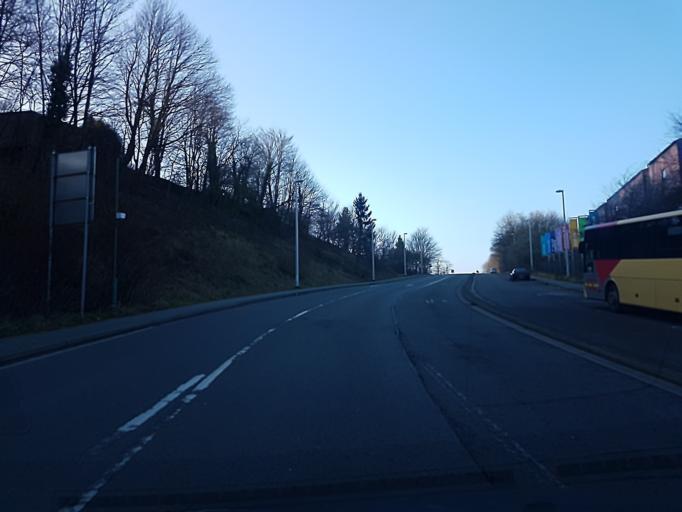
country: BE
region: Wallonia
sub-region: Province de Liege
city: Verviers
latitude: 50.5932
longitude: 5.8714
